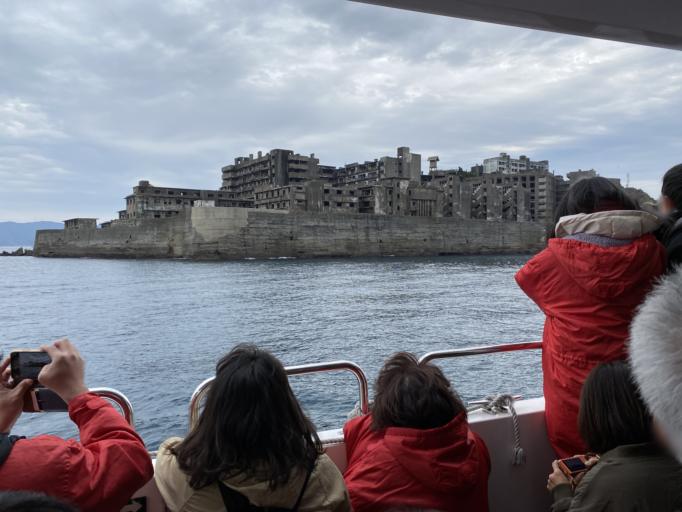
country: JP
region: Nagasaki
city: Nagasaki-shi
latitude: 32.6305
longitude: 129.7380
